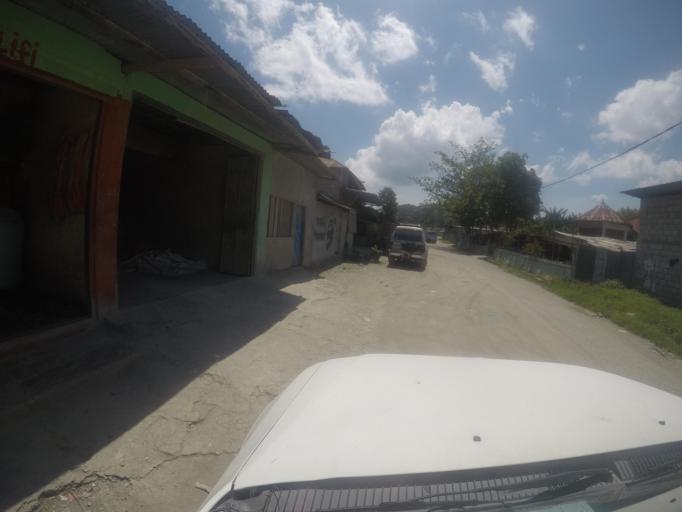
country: TL
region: Ermera
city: Gleno
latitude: -8.7222
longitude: 125.4364
